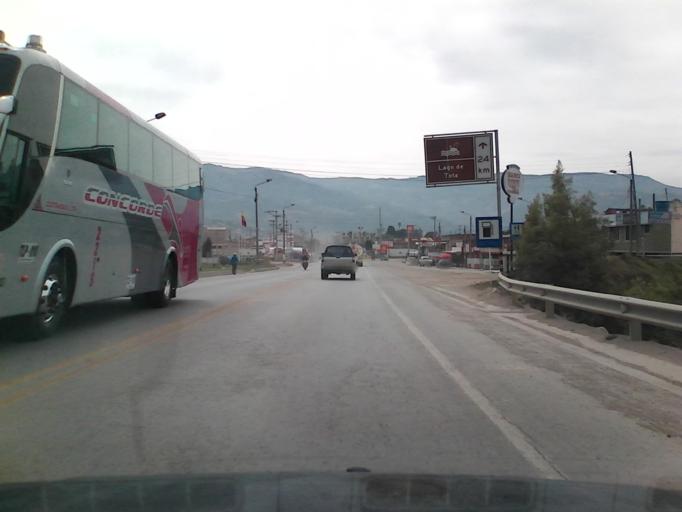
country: CO
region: Boyaca
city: Sogamoso
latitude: 5.7253
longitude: -72.9443
